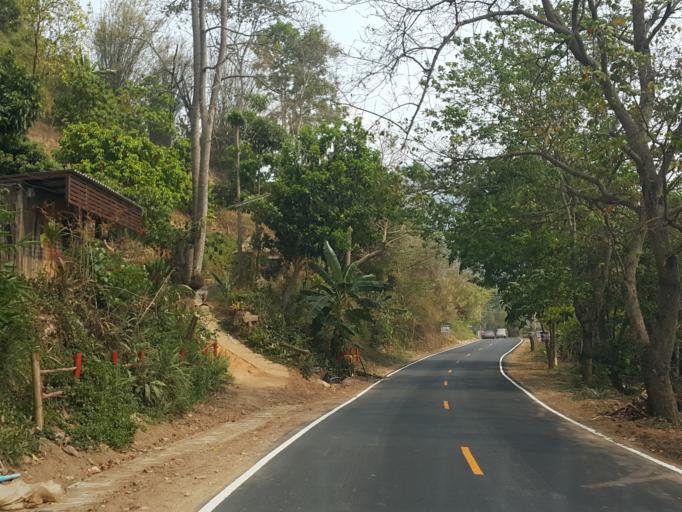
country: TH
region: Chiang Mai
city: Samoeng
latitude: 18.8990
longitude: 98.8315
